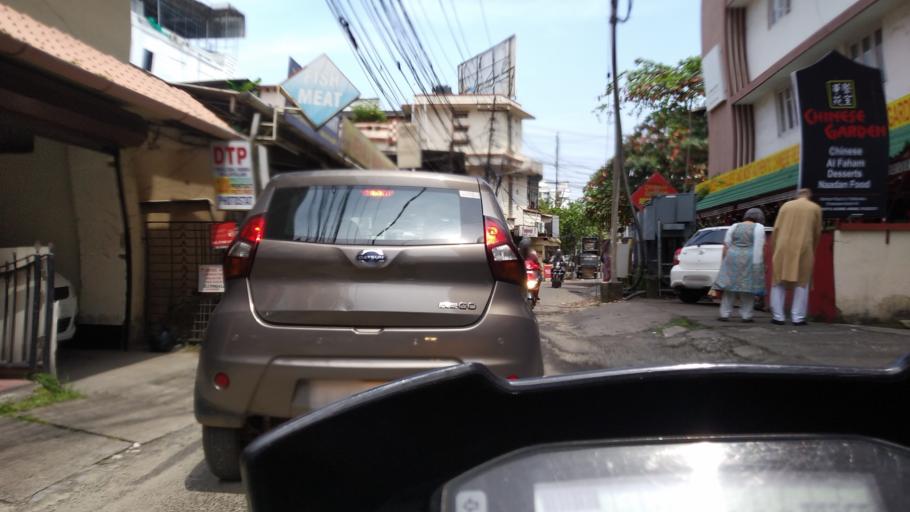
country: IN
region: Kerala
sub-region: Ernakulam
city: Cochin
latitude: 9.9655
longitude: 76.2859
